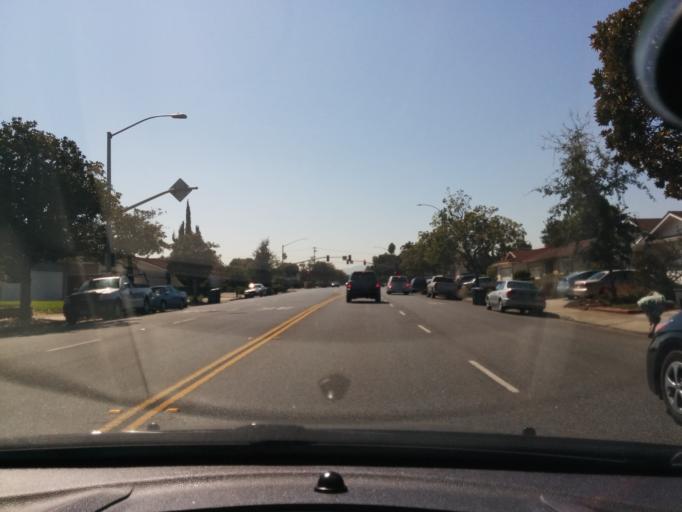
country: US
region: California
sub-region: Santa Clara County
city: Sunnyvale
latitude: 37.3638
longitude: -122.0143
